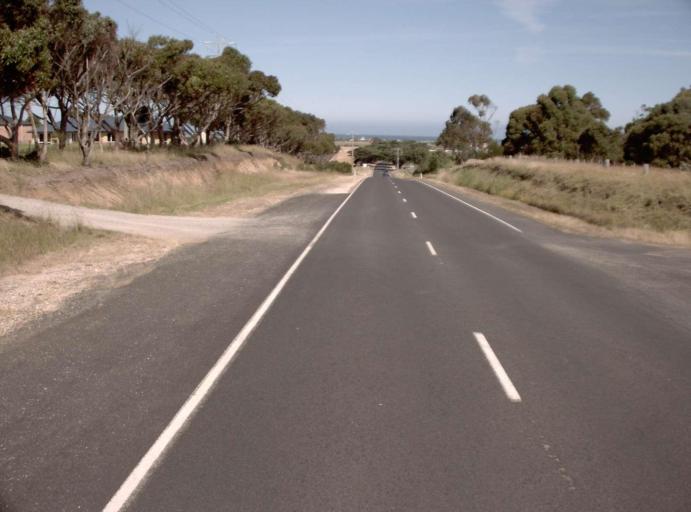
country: AU
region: Victoria
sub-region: Wellington
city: Sale
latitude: -38.3611
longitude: 147.1798
